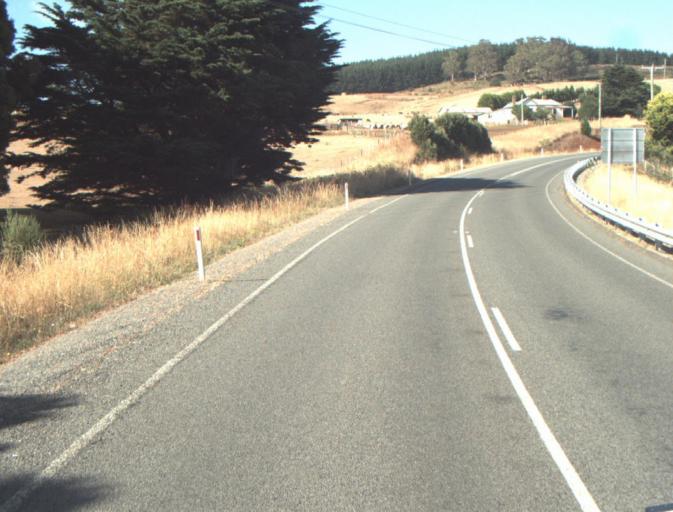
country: AU
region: Tasmania
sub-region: Dorset
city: Bridport
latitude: -41.1643
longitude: 147.2402
